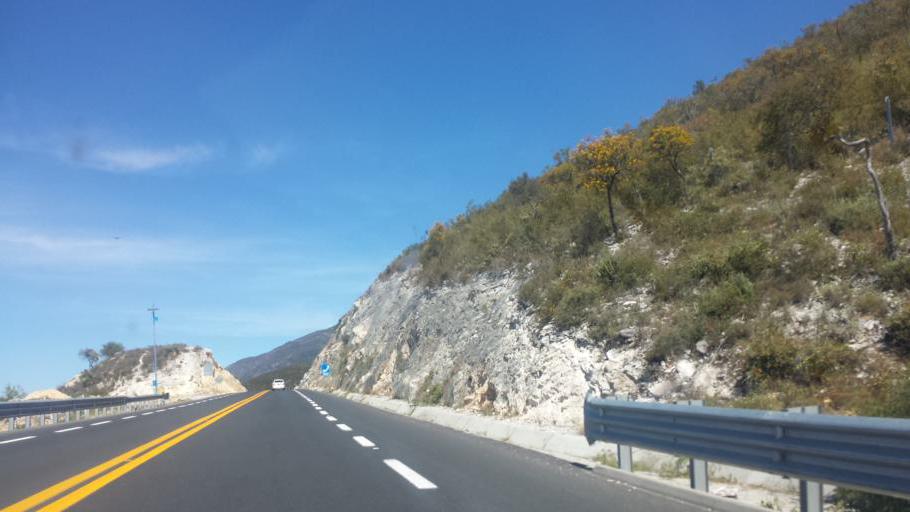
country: MX
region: Puebla
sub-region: San Jose Miahuatlan
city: San Pedro Tetitlan
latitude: 18.0092
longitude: -97.3558
